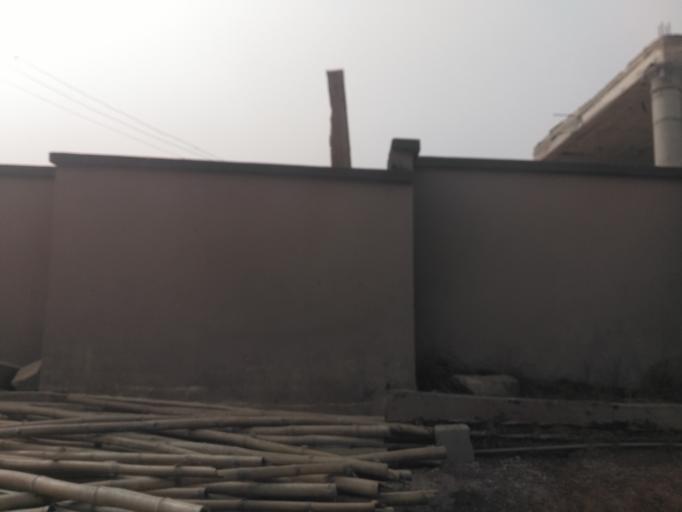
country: GH
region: Ashanti
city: Kumasi
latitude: 6.6641
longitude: -1.6141
